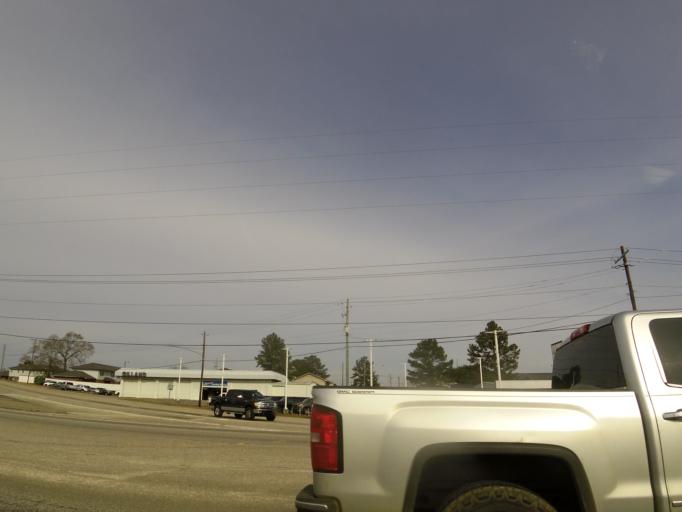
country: US
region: Alabama
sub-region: Dale County
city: Ozark
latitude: 31.4328
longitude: -85.6297
